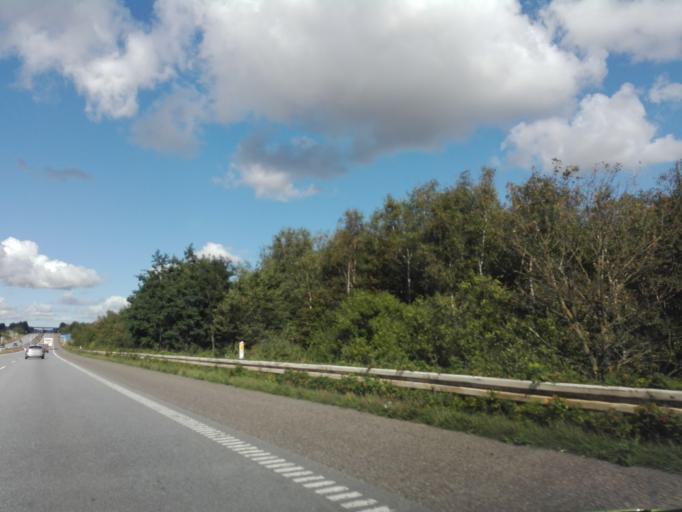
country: DK
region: Central Jutland
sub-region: Randers Kommune
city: Randers
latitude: 56.4780
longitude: 9.9816
